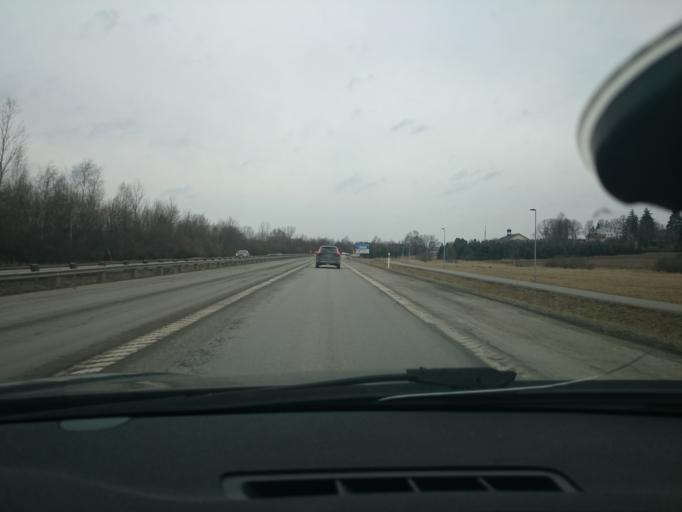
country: SE
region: OEstergoetland
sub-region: Norrkopings Kommun
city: Norrkoping
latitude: 58.5582
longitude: 16.2309
